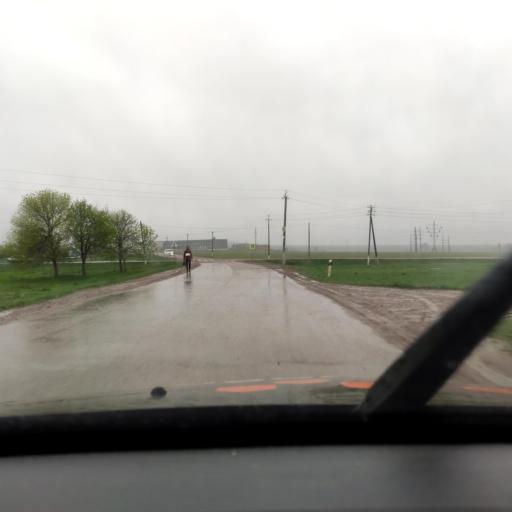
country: RU
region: Bashkortostan
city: Asanovo
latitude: 54.7649
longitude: 55.4880
